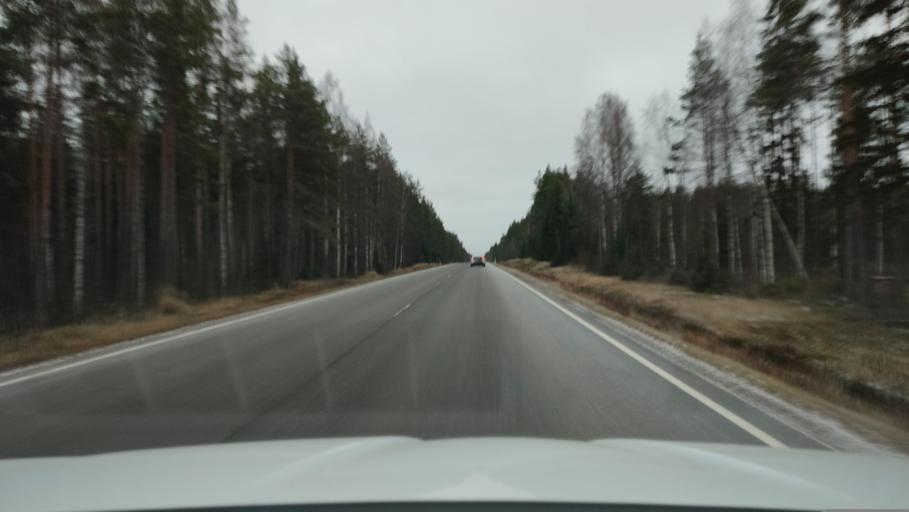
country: FI
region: Ostrobothnia
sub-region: Sydosterbotten
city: Naerpes
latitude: 62.5850
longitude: 21.4968
